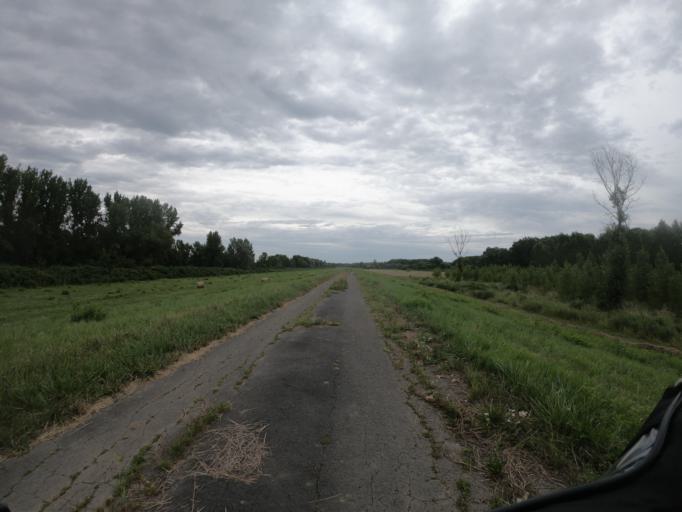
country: HU
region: Hajdu-Bihar
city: Egyek
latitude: 47.6977
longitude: 20.9100
